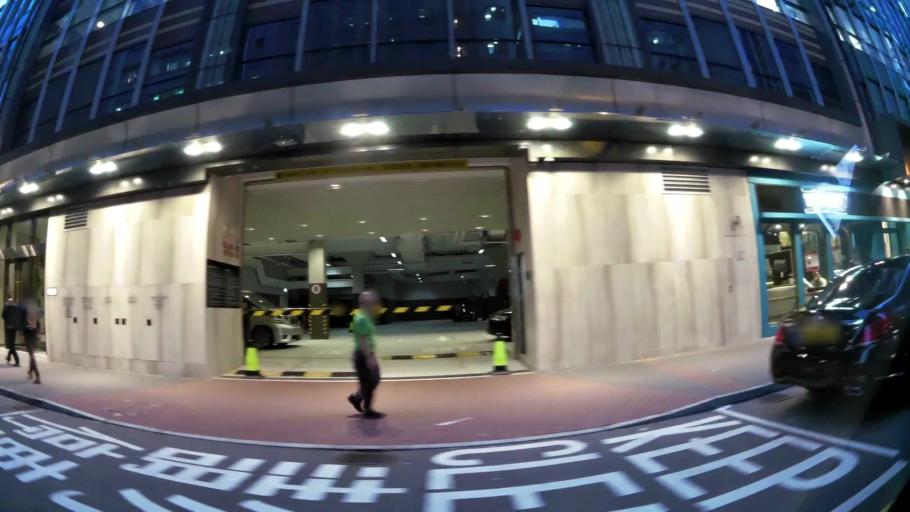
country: HK
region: Kowloon City
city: Kowloon
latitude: 22.3089
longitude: 114.2240
